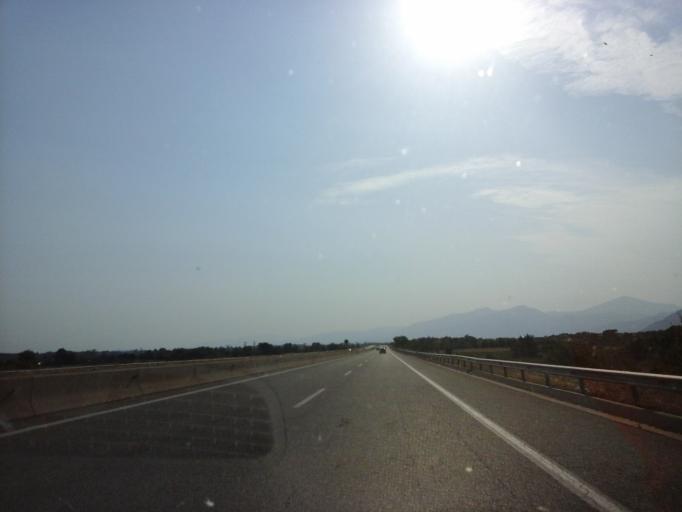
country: GR
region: East Macedonia and Thrace
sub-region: Nomos Xanthis
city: Selero
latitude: 41.1199
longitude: 25.0561
